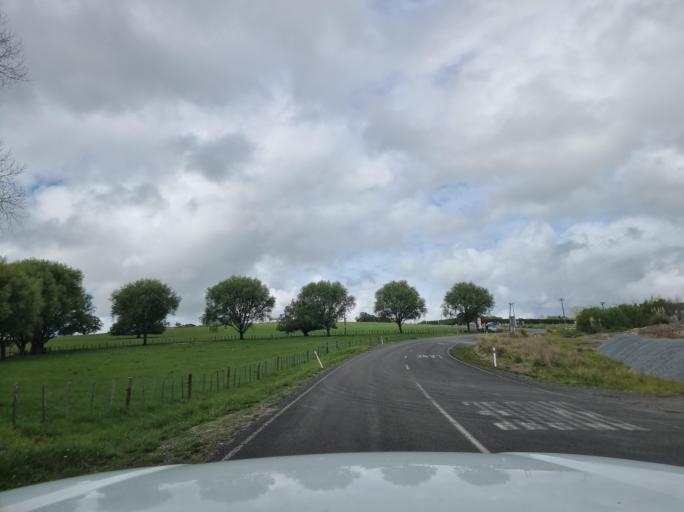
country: NZ
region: Northland
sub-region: Whangarei
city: Ruakaka
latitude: -36.1246
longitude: 174.1890
